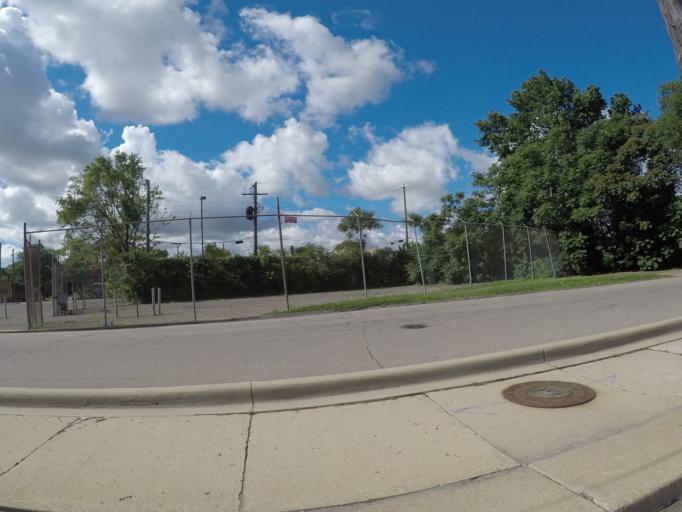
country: US
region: Michigan
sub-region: Wayne County
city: Hamtramck
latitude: 42.4188
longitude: -83.0550
